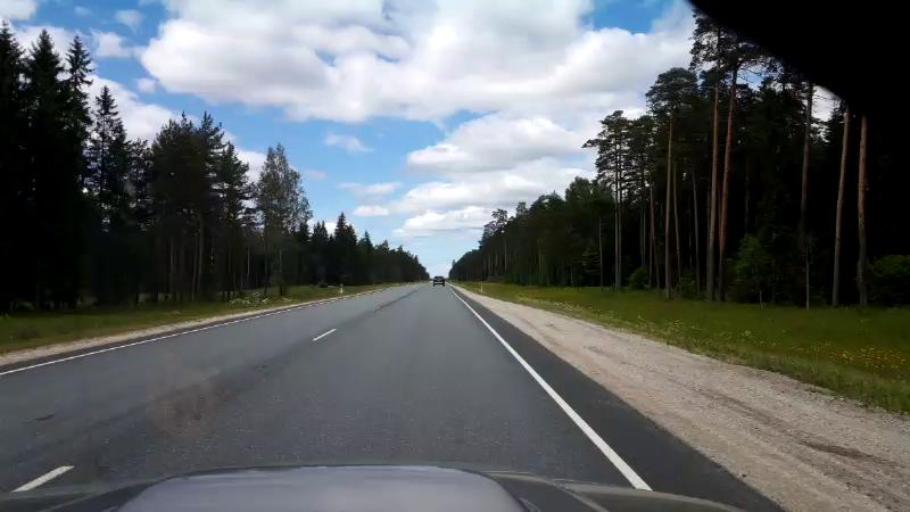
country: EE
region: Raplamaa
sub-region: Maerjamaa vald
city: Marjamaa
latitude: 59.0113
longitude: 24.4559
